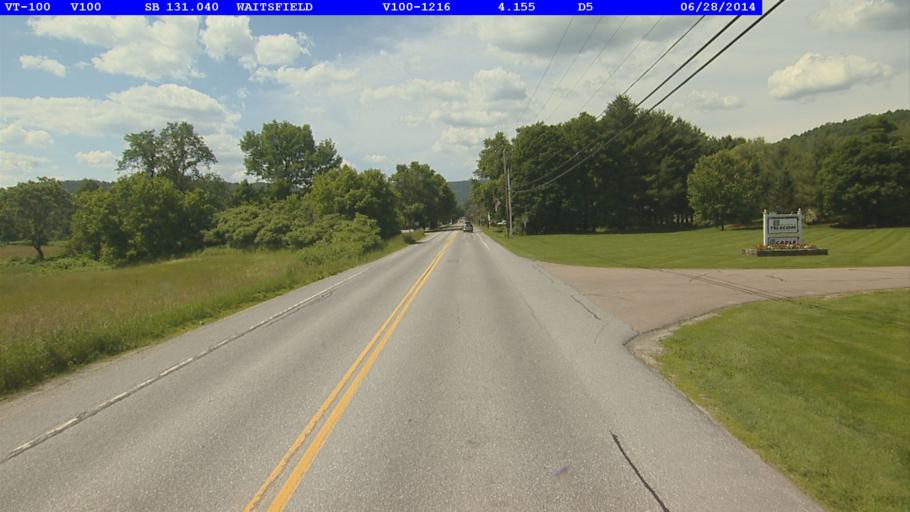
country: US
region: Vermont
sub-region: Washington County
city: Waterbury
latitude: 44.1961
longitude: -72.8185
